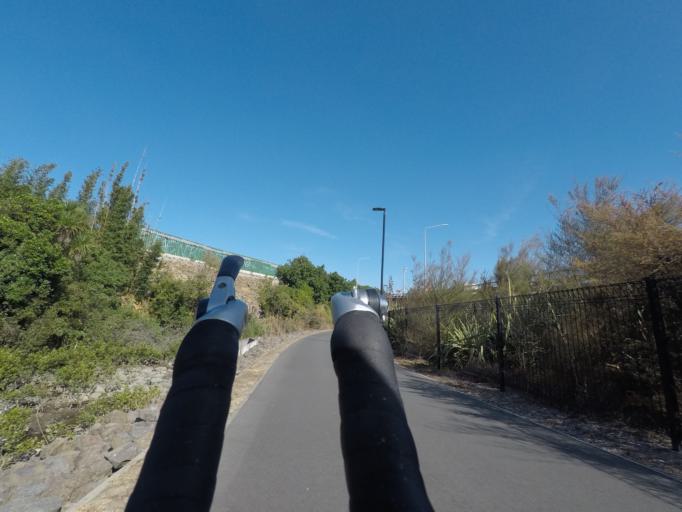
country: NZ
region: Auckland
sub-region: Auckland
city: Rosebank
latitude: -36.8703
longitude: 174.6737
